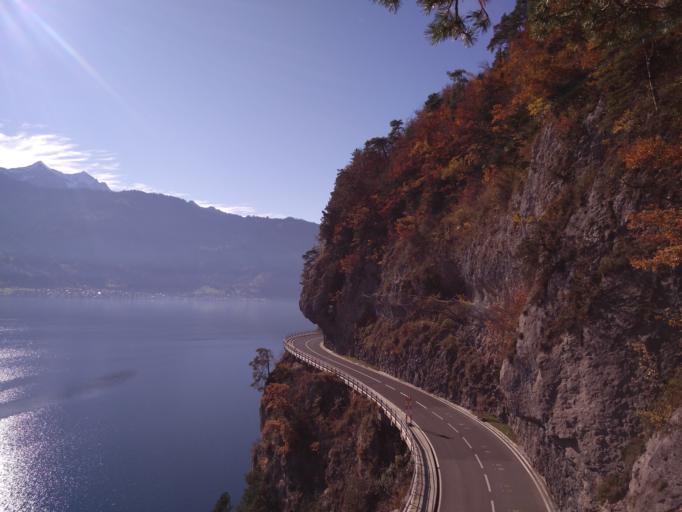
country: CH
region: Bern
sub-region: Interlaken-Oberhasli District
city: Beatenberg
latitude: 46.6856
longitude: 7.7883
